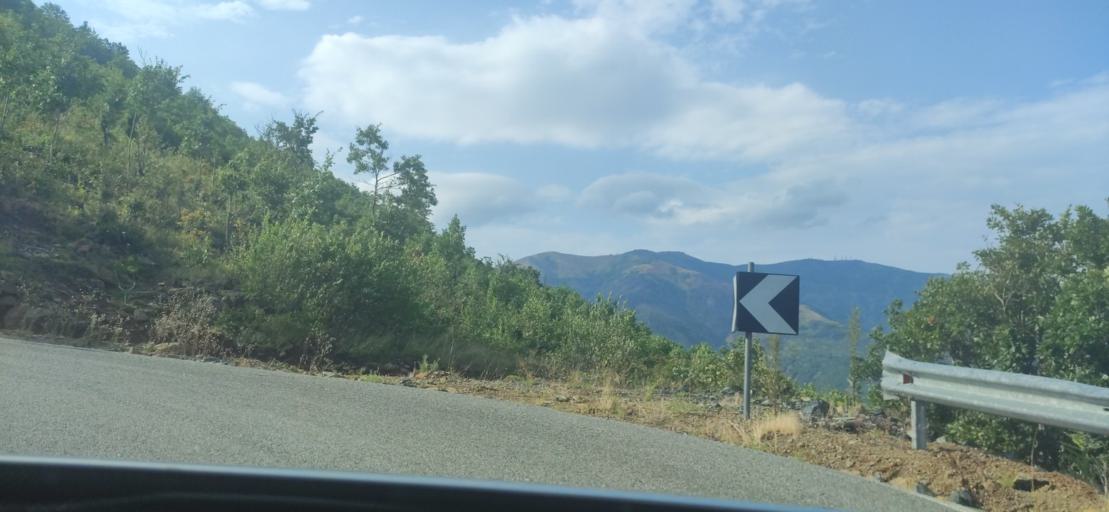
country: AL
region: Shkoder
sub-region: Rrethi i Pukes
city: Iballe
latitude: 42.1686
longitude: 20.0028
